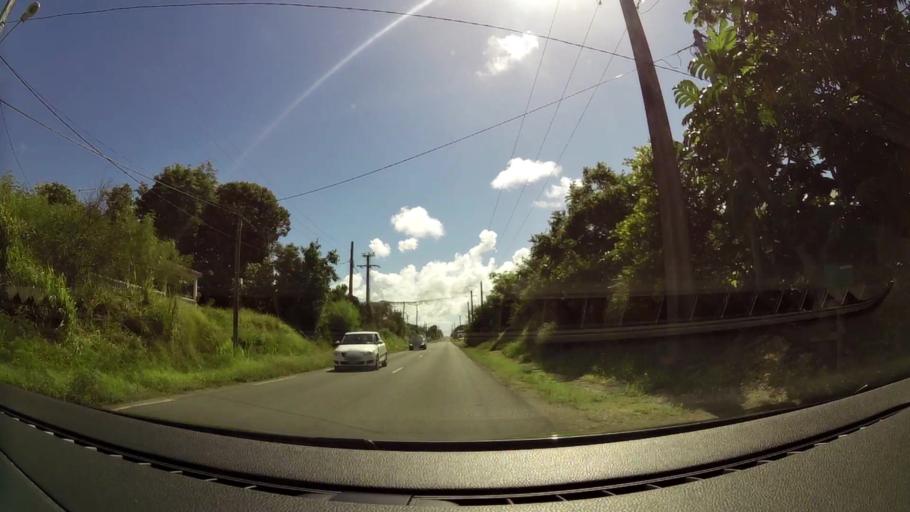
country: GP
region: Guadeloupe
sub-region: Guadeloupe
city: Petit-Canal
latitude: 16.4106
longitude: -61.4690
